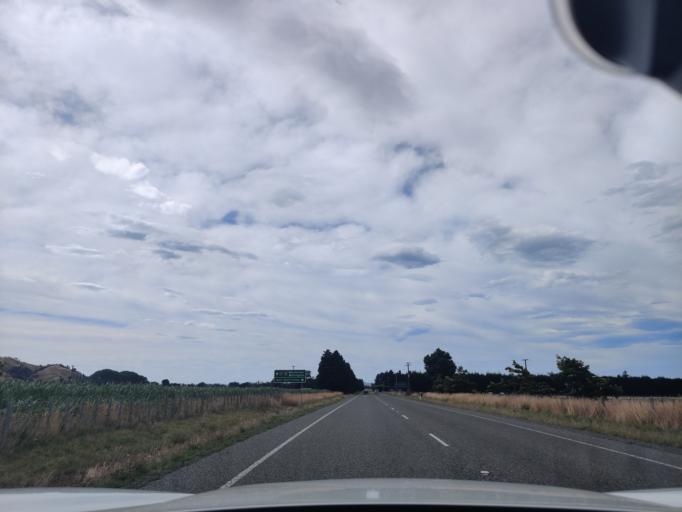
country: NZ
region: Wellington
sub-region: Masterton District
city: Masterton
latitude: -40.8567
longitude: 175.6395
